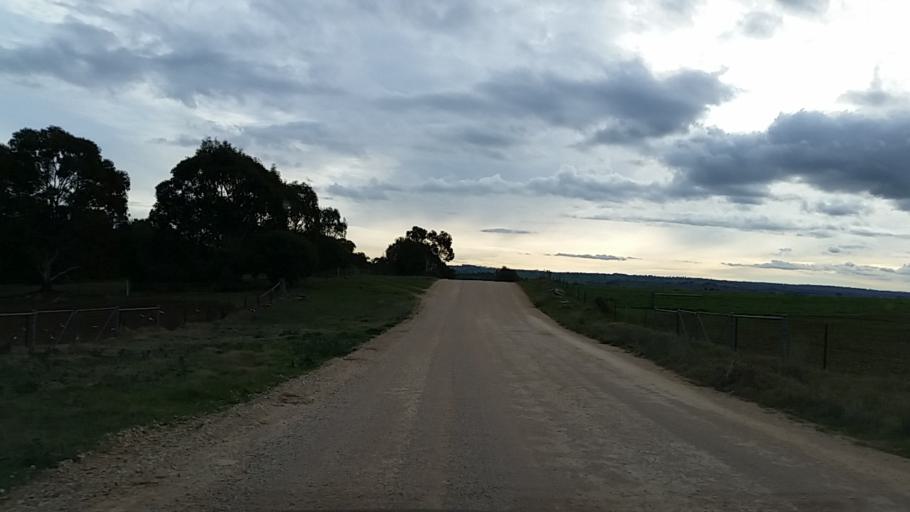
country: AU
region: South Australia
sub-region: Mount Barker
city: Callington
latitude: -34.9991
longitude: 139.0443
